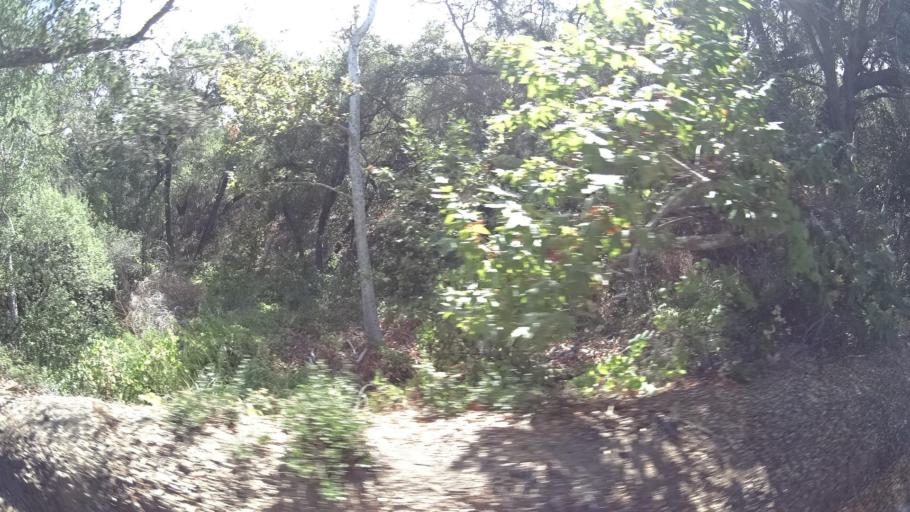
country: US
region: California
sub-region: San Diego County
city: Fallbrook
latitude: 33.4193
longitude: -117.2349
